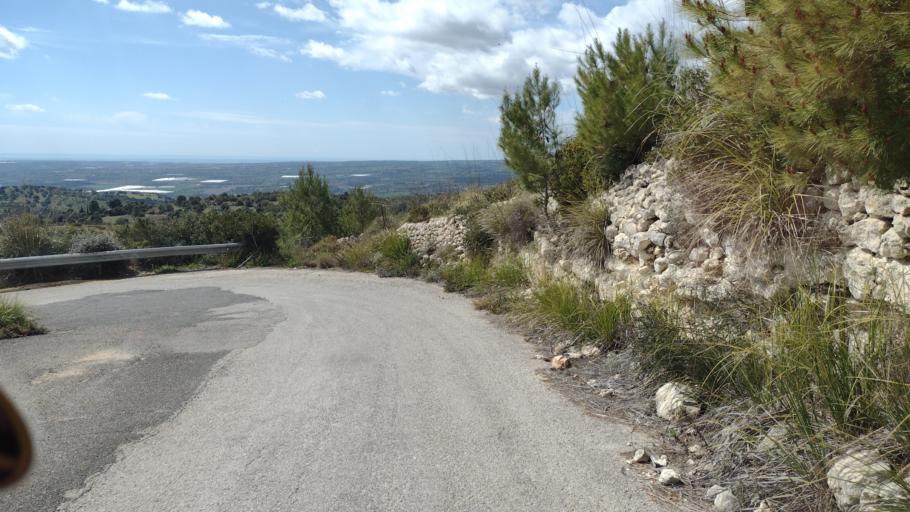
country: IT
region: Sicily
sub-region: Provincia di Siracusa
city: Noto
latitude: 36.9123
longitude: 14.9792
